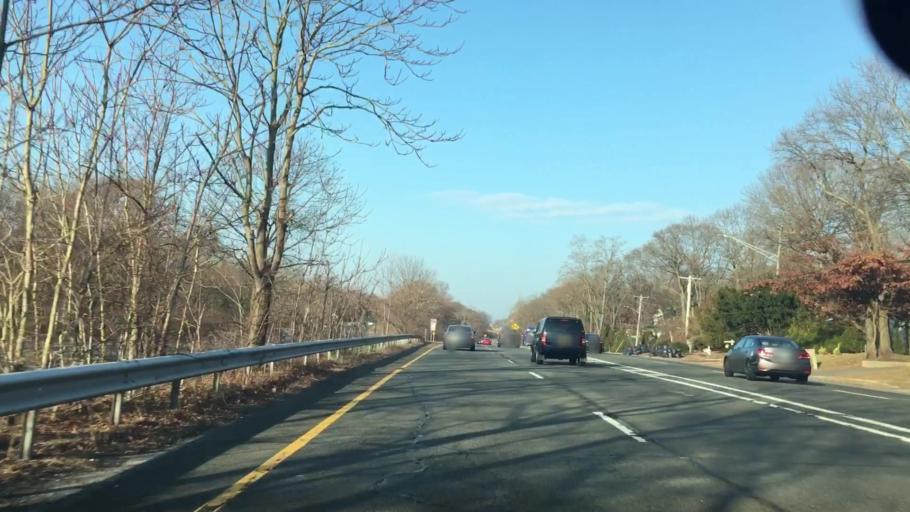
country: US
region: New York
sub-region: Suffolk County
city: Commack
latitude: 40.8292
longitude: -73.2495
